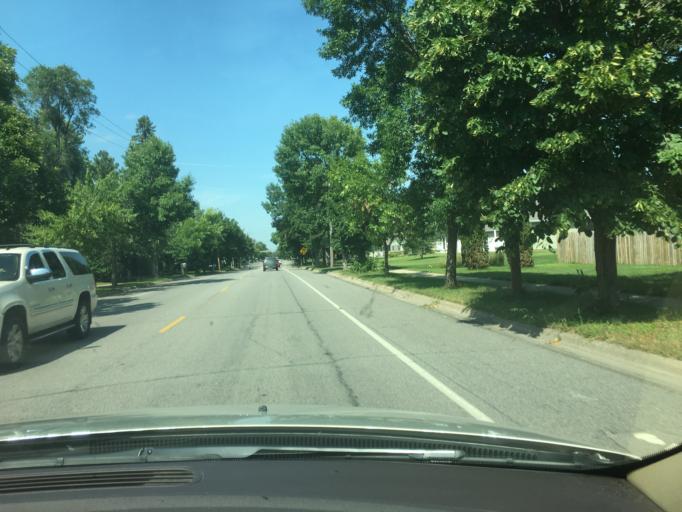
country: US
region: Minnesota
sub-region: Stearns County
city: Saint Cloud
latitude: 45.5396
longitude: -94.1616
